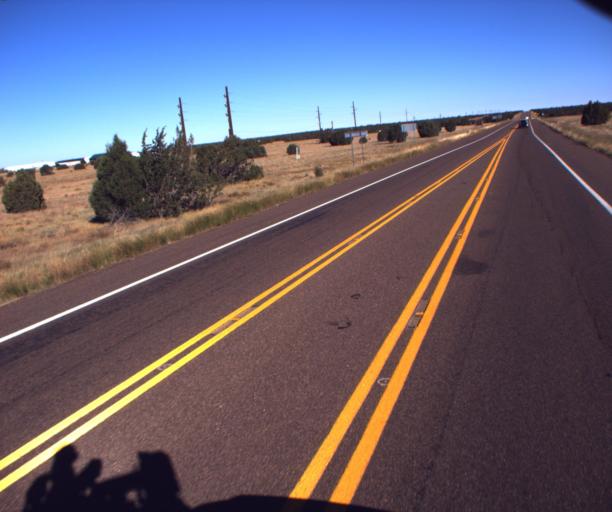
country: US
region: Arizona
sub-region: Navajo County
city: Show Low
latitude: 34.2646
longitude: -110.0209
